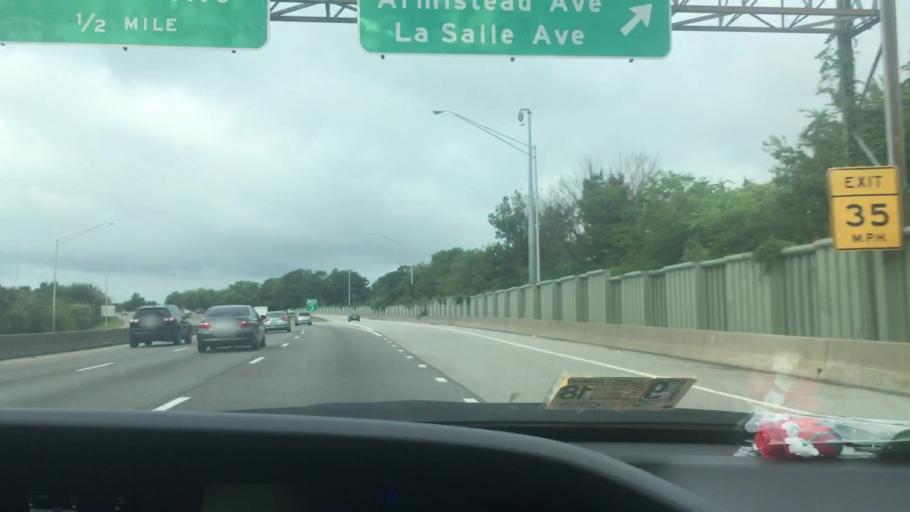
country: US
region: Virginia
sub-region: City of Hampton
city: Hampton
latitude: 37.0350
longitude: -76.3565
